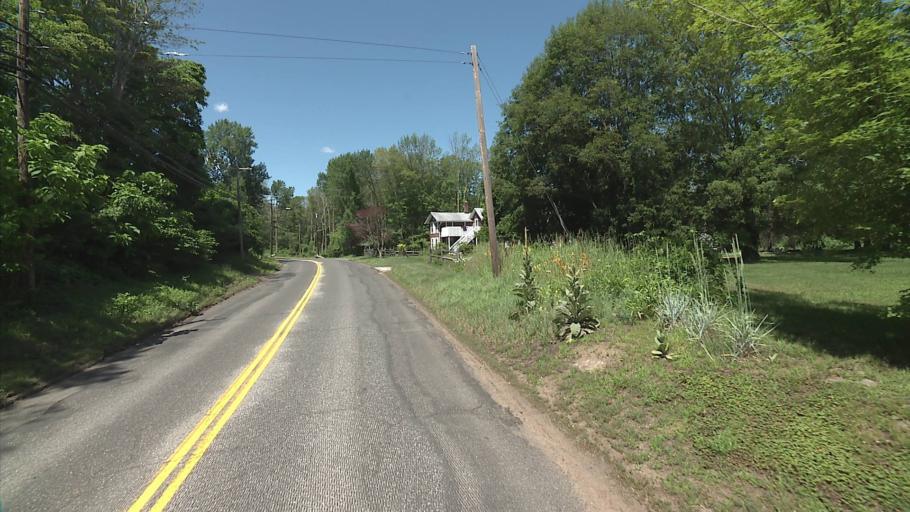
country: US
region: Connecticut
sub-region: Middlesex County
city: East Hampton
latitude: 41.5656
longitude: -72.4720
